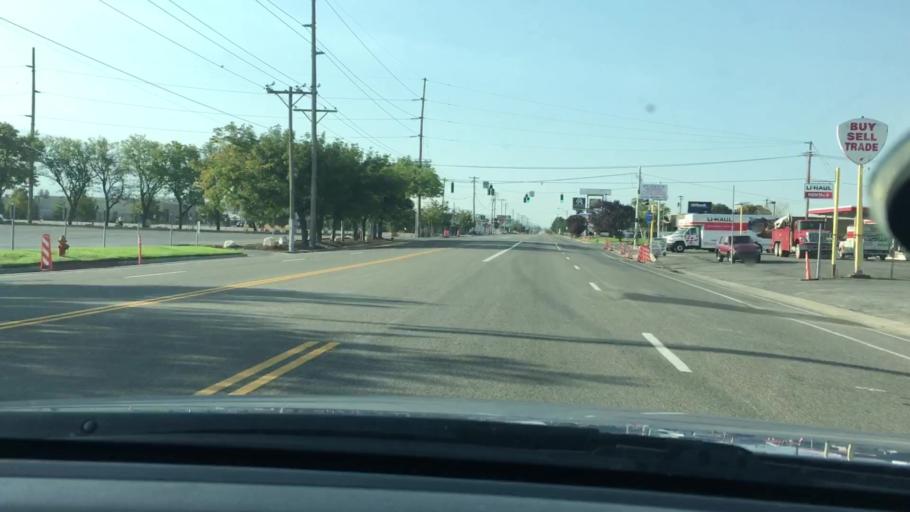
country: US
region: Utah
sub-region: Salt Lake County
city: South Salt Lake
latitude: 40.7135
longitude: -111.8998
